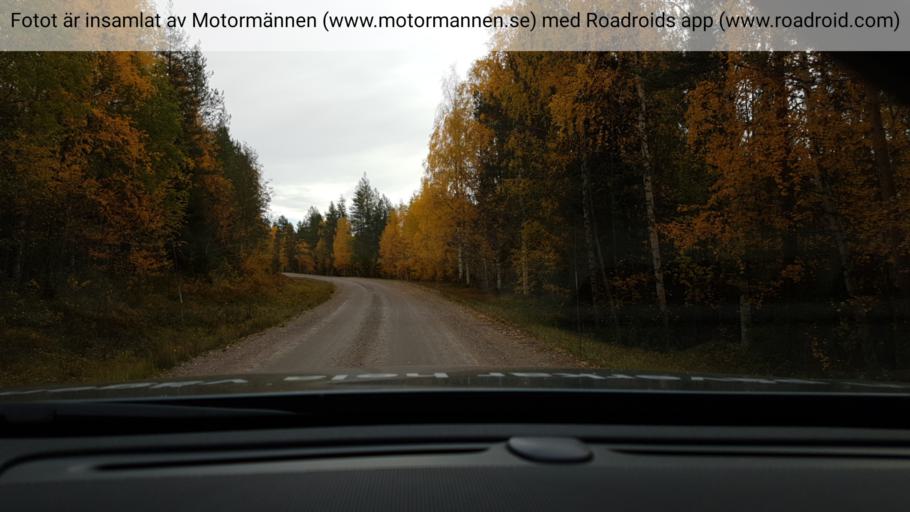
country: SE
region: Norrbotten
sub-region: Overkalix Kommun
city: OEverkalix
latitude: 66.2741
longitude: 22.9880
